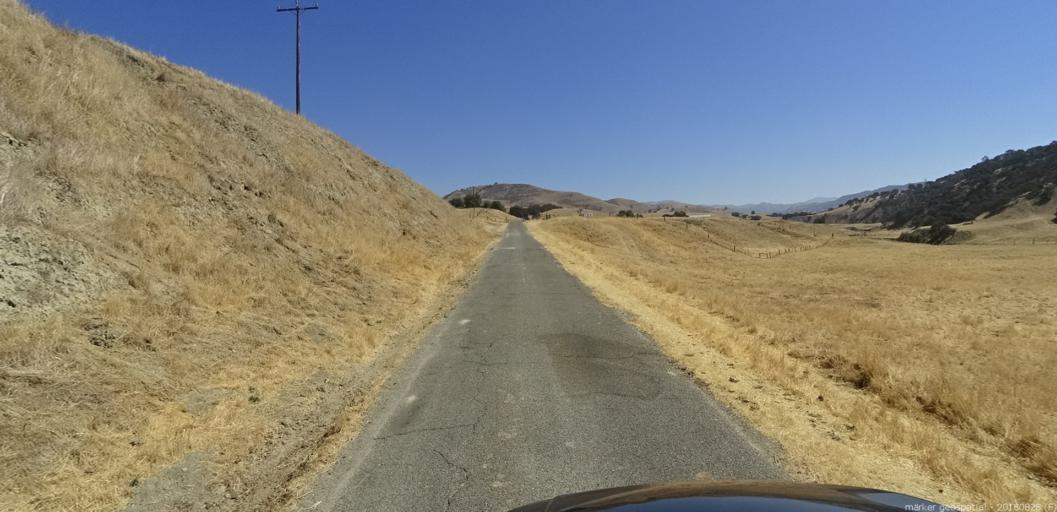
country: US
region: California
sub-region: San Luis Obispo County
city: San Miguel
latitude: 36.0648
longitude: -120.7877
